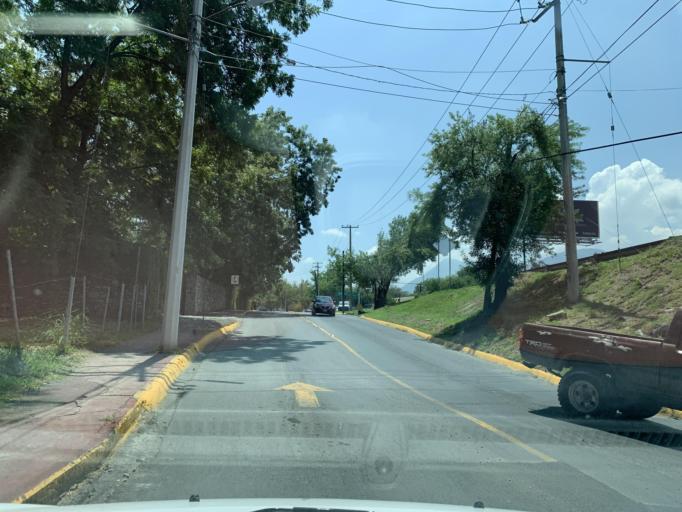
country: MX
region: Nuevo Leon
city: Santiago
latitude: 25.4012
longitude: -100.1316
